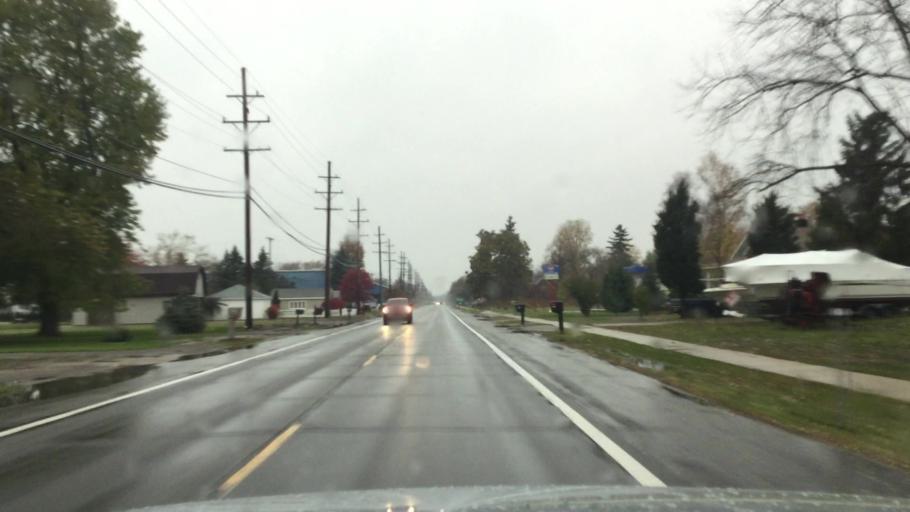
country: US
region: Michigan
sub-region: Saint Clair County
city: Pearl Beach
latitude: 42.6248
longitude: -82.5906
